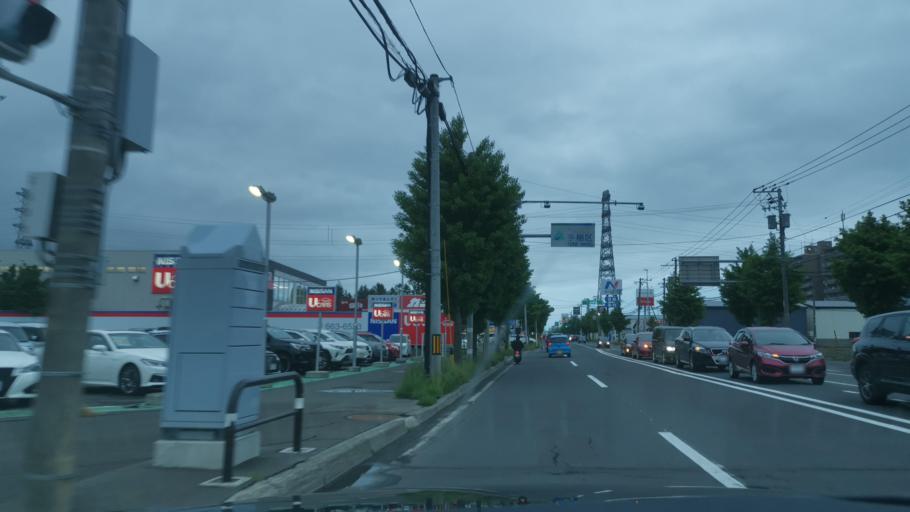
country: JP
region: Hokkaido
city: Sapporo
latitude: 43.1094
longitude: 141.2779
